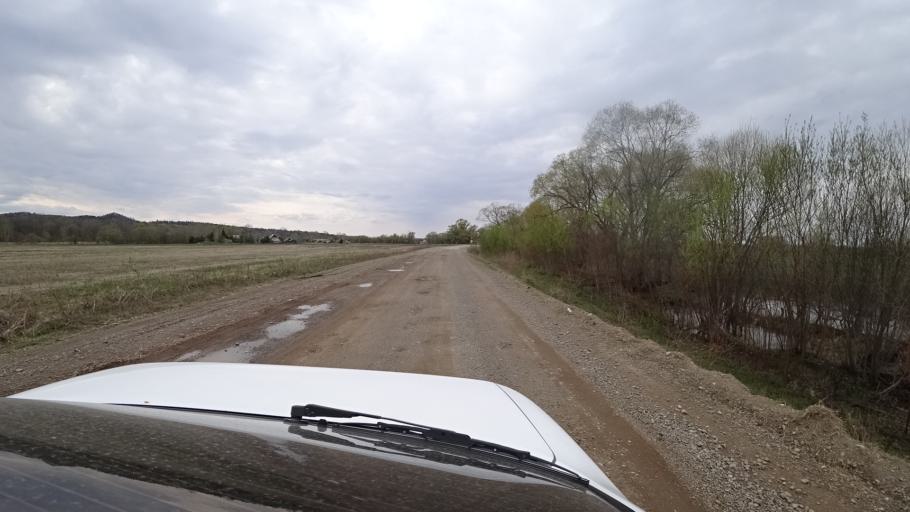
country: RU
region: Primorskiy
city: Novopokrovka
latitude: 45.4911
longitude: 134.4556
